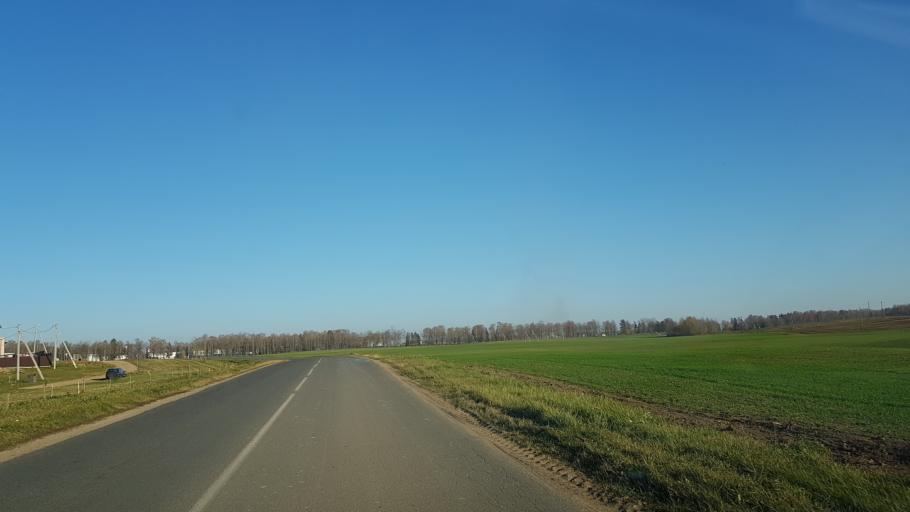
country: BY
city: Fanipol
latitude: 53.7247
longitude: 27.3237
